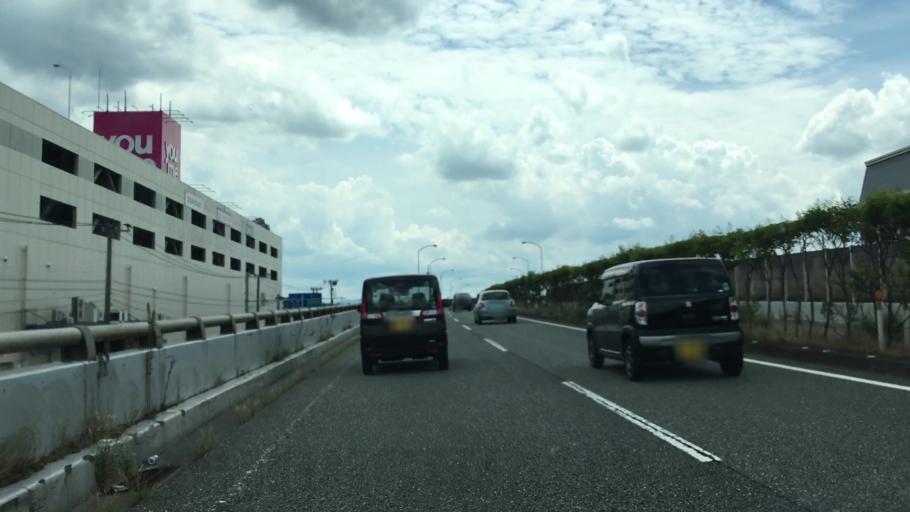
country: JP
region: Fukuoka
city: Chikushino-shi
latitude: 33.4846
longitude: 130.5373
